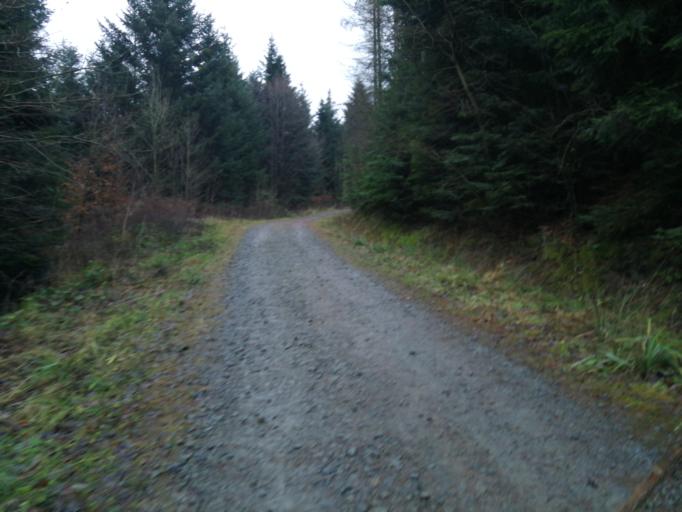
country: PL
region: Lesser Poland Voivodeship
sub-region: Powiat myslenicki
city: Myslenice
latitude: 49.8202
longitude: 19.9609
